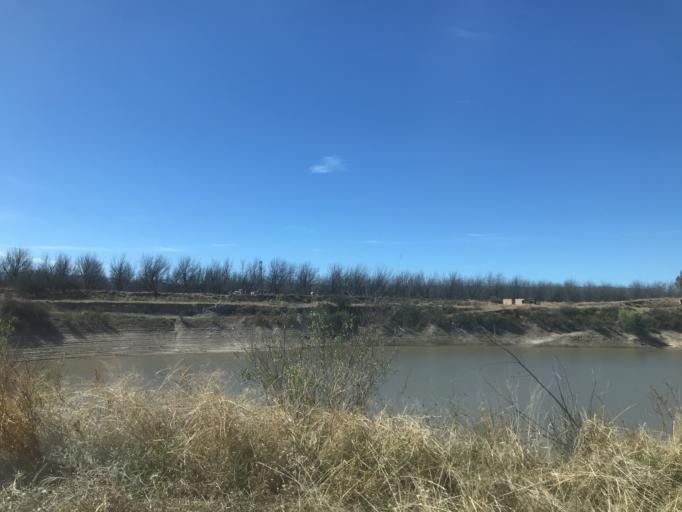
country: MX
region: Durango
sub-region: Durango
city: Sebastian Lerdo de Tejada
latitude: 23.9743
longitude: -104.6182
